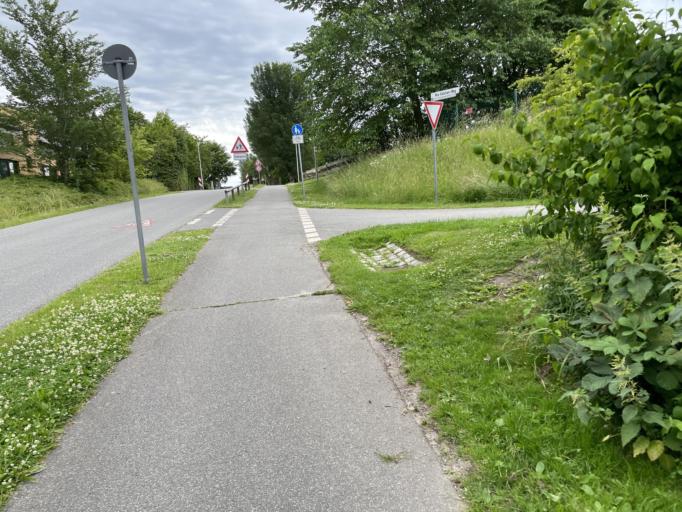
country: DE
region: Schleswig-Holstein
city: Mildstedt
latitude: 54.4692
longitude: 9.0865
